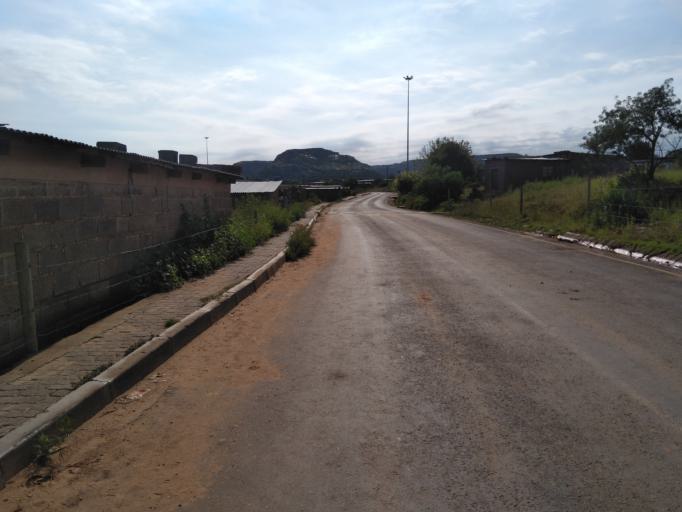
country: LS
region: Butha-Buthe
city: Butha-Buthe
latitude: -28.7745
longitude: 28.2471
